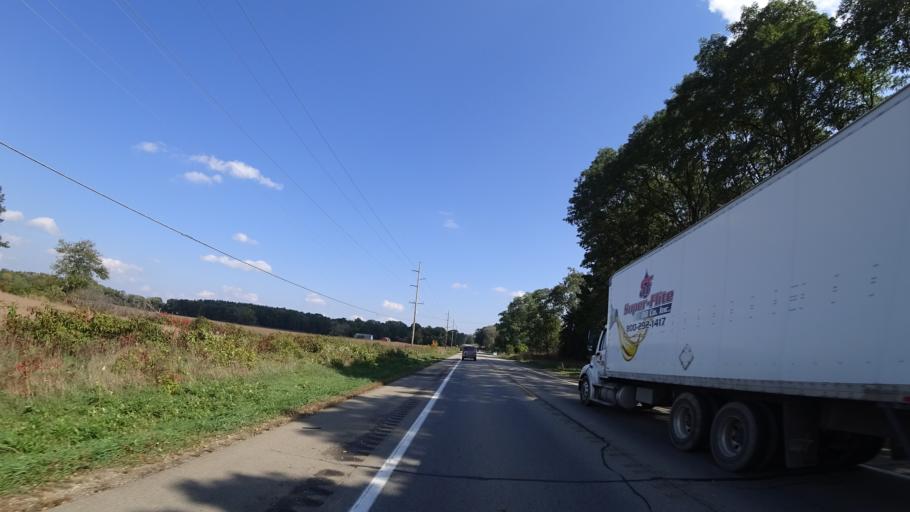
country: US
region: Michigan
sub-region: Jackson County
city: Concord
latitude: 42.1641
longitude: -84.6883
